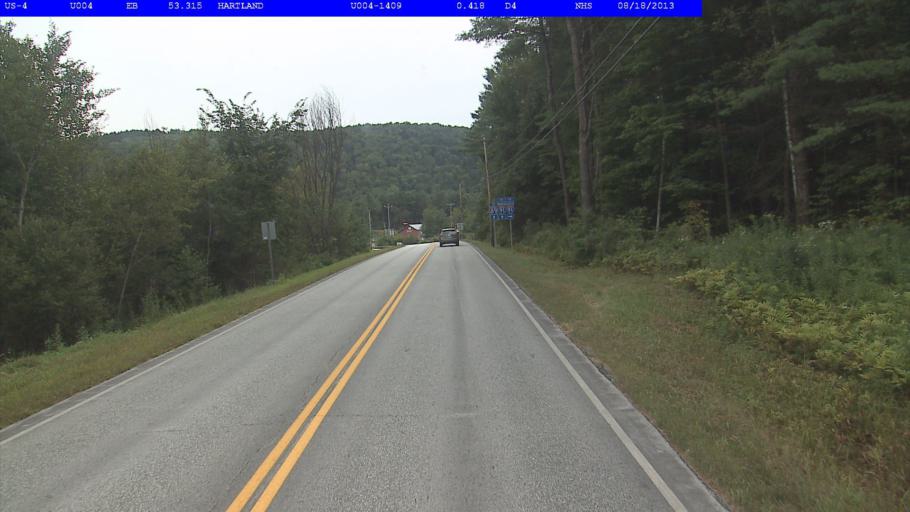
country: US
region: Vermont
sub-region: Windsor County
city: Woodstock
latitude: 43.6274
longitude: -72.4605
